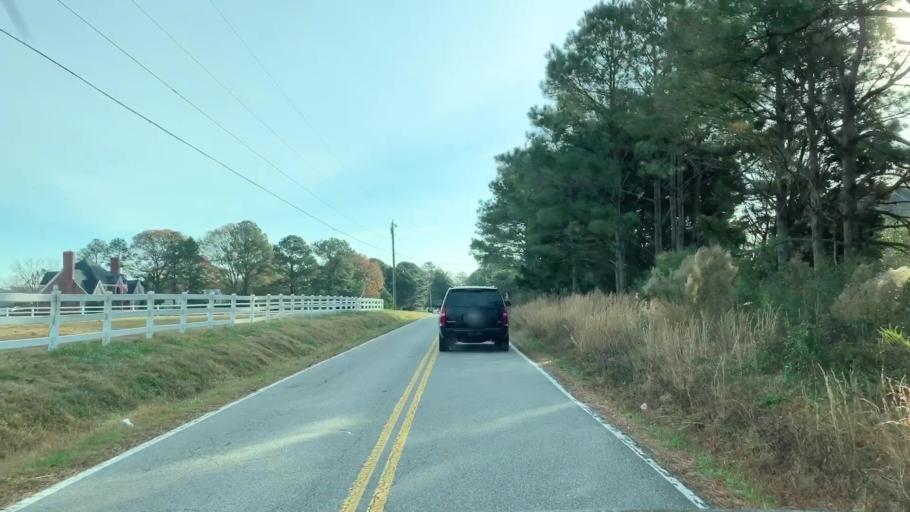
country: US
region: Virginia
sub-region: City of Virginia Beach
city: Virginia Beach
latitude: 36.6865
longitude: -75.9985
